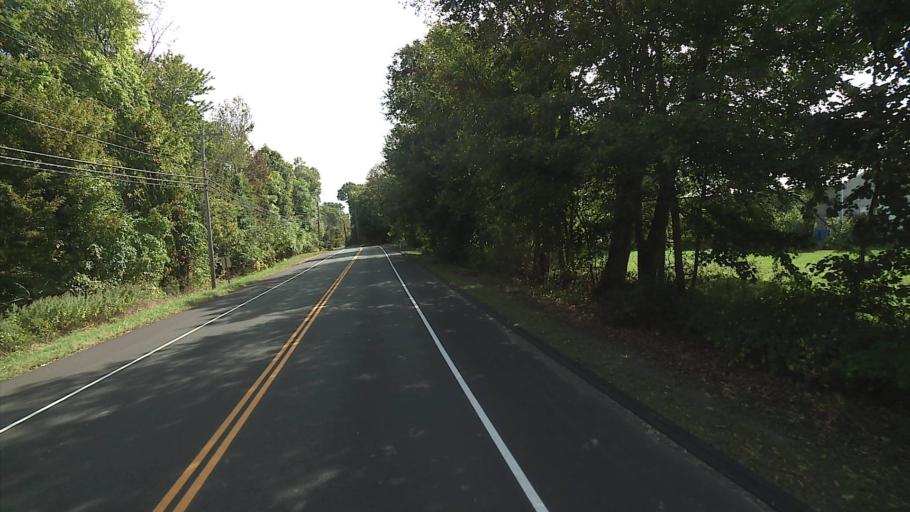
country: US
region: Connecticut
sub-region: Fairfield County
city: Newtown
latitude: 41.3911
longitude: -73.2219
